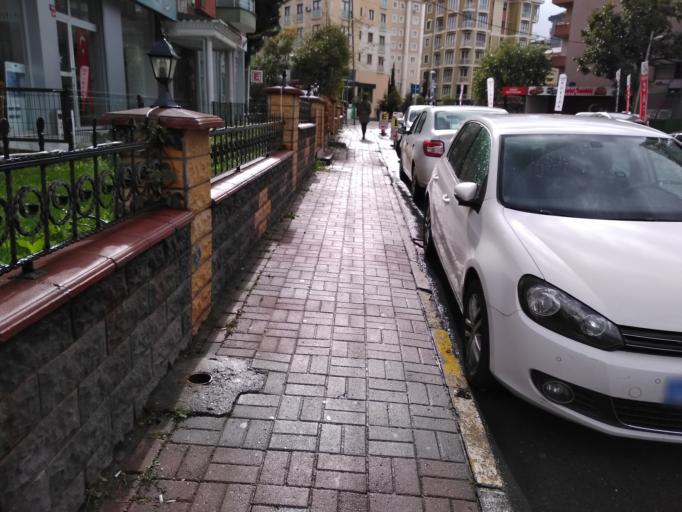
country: TR
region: Istanbul
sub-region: Atasehir
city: Atasehir
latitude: 40.9824
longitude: 29.1193
